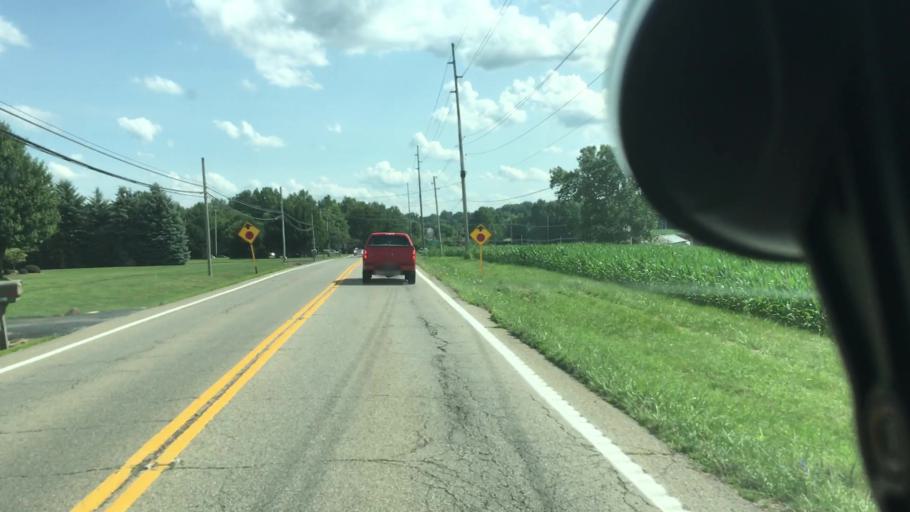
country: US
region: Ohio
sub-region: Mahoning County
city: Canfield
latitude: 40.9906
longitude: -80.7971
